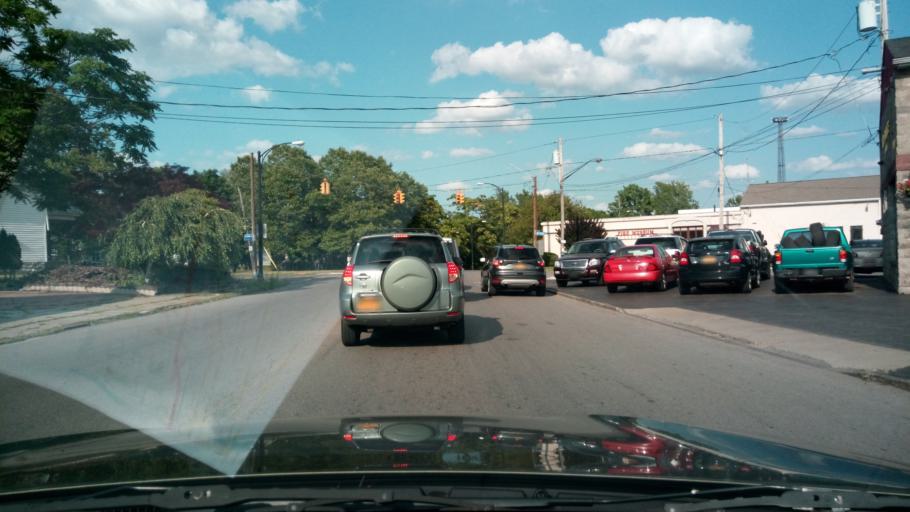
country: US
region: New York
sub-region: Erie County
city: Sloan
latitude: 42.8849
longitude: -78.8030
